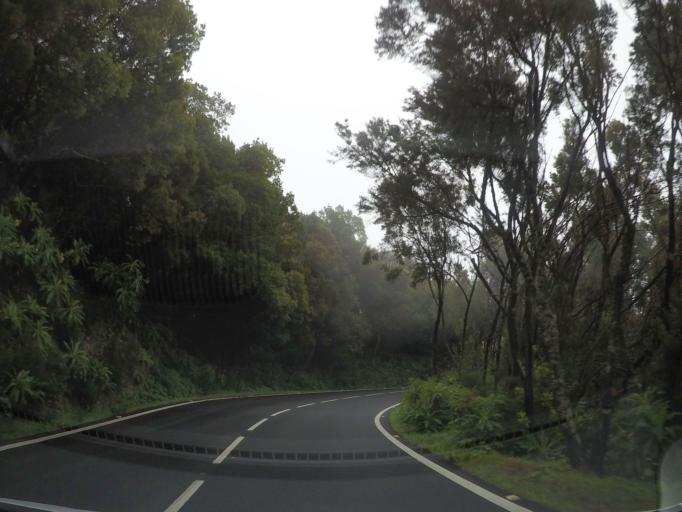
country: ES
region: Canary Islands
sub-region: Provincia de Santa Cruz de Tenerife
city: Vallehermosa
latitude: 28.1268
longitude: -17.2627
